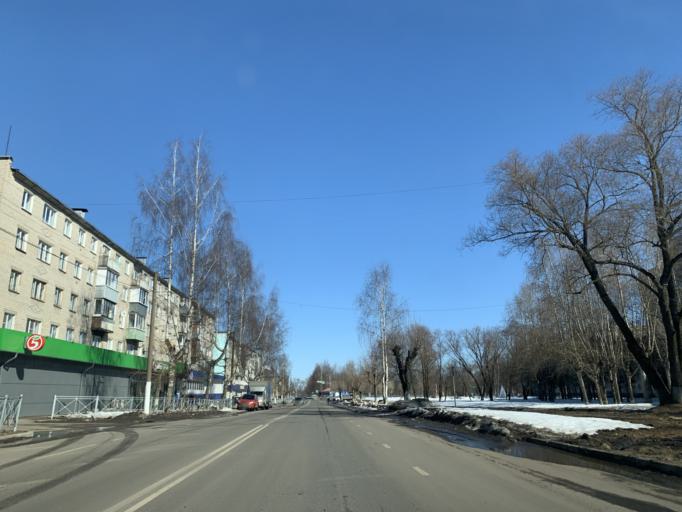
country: RU
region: Jaroslavl
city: Tutayev
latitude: 57.8683
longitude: 39.5119
